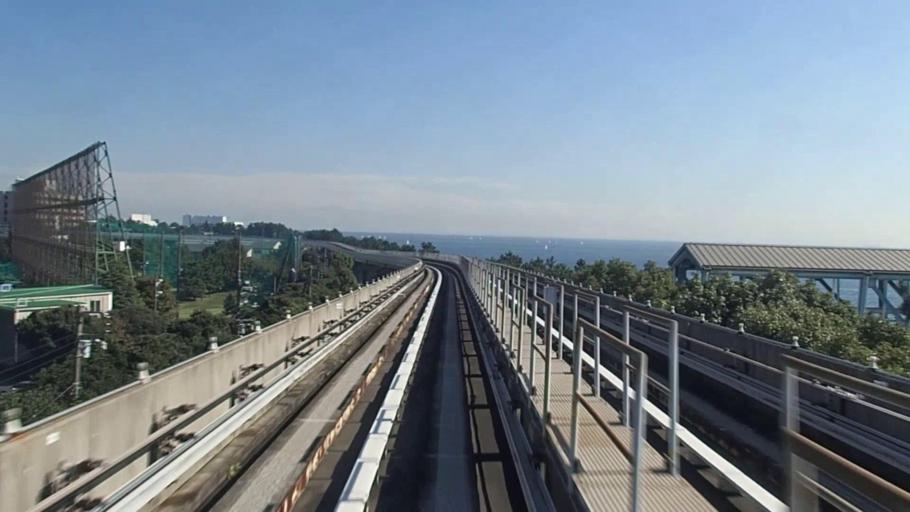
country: JP
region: Kanagawa
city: Yokosuka
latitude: 35.3401
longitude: 139.6458
